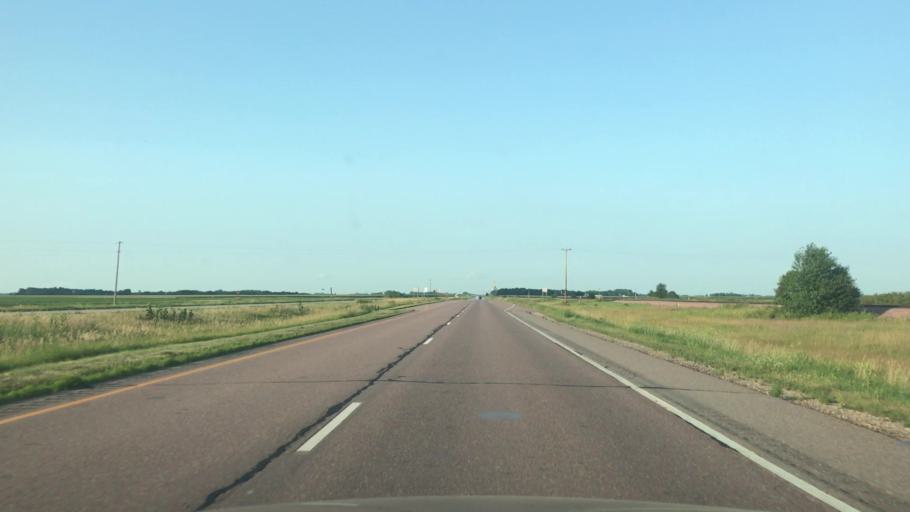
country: US
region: Minnesota
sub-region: Nobles County
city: Worthington
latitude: 43.7457
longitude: -95.3990
